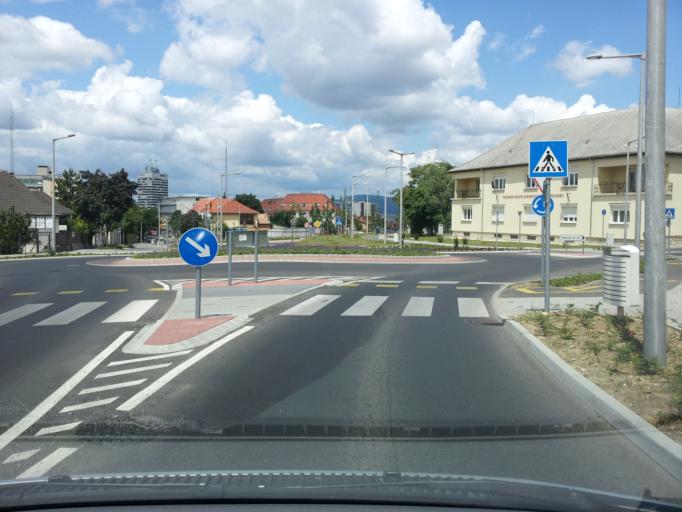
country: HU
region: Veszprem
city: Veszprem
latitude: 47.0881
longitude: 17.9170
